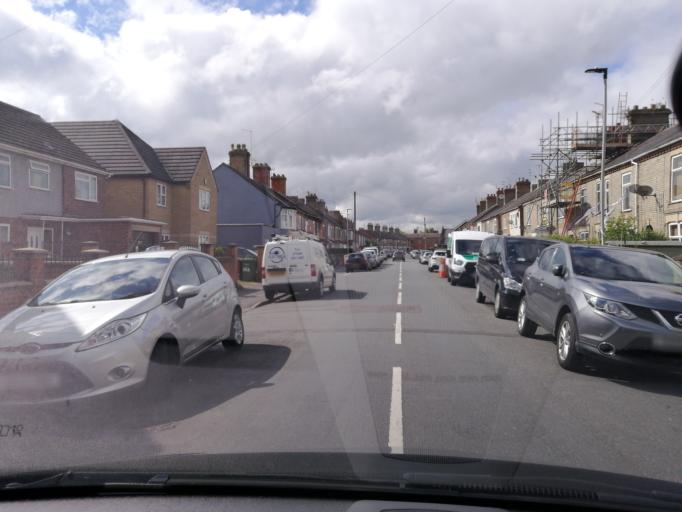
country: GB
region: England
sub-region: Peterborough
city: Peterborough
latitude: 52.5613
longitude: -0.2526
